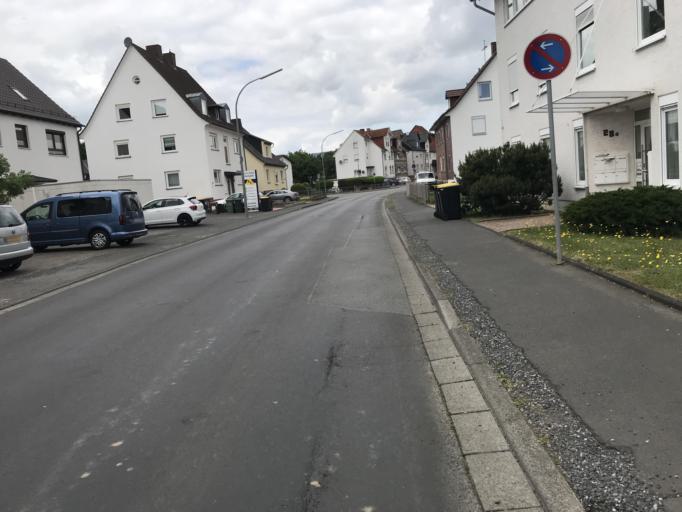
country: DE
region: Hesse
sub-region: Regierungsbezirk Kassel
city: Baunatal
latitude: 51.2505
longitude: 9.3835
